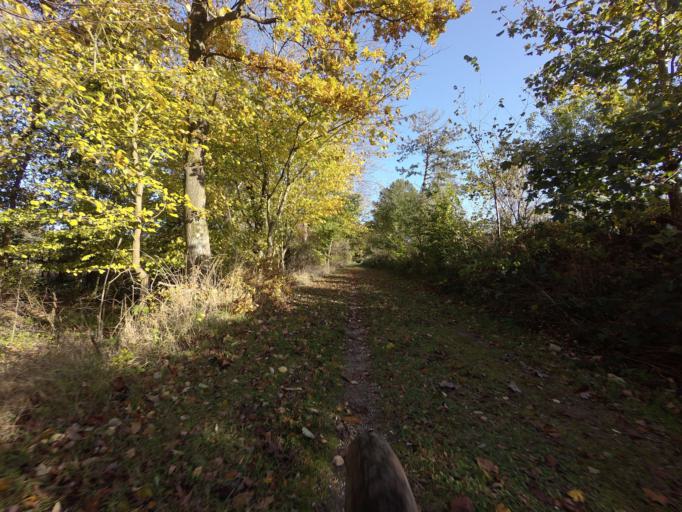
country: DK
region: Central Jutland
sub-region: Norddjurs Kommune
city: Grenaa
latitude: 56.4957
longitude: 10.7209
